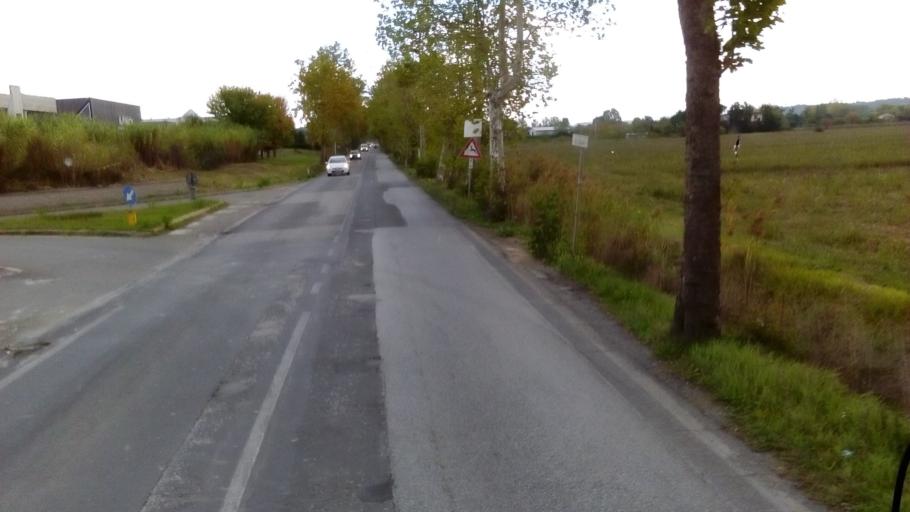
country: IT
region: Tuscany
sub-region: Province of Florence
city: Castelfiorentino
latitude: 43.5882
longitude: 10.9910
